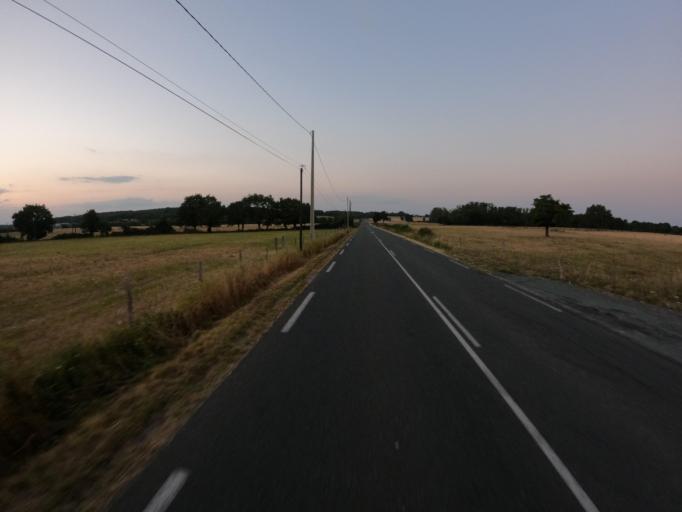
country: FR
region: Pays de la Loire
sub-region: Departement de Maine-et-Loire
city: Cande
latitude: 47.5956
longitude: -0.9996
